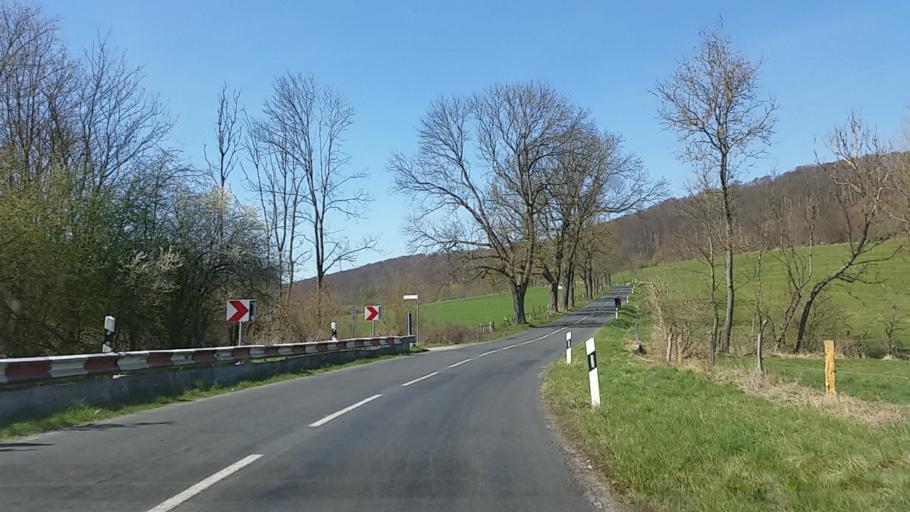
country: DE
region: Lower Saxony
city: Erkerode
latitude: 52.2071
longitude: 10.7492
